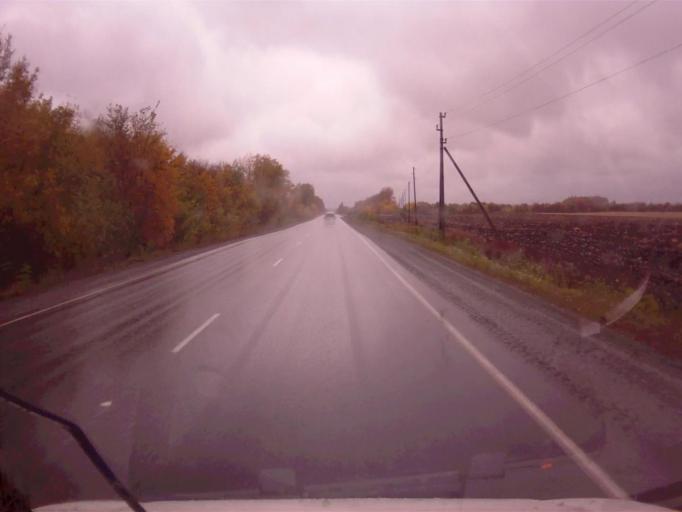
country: RU
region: Chelyabinsk
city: Argayash
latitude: 55.4321
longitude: 60.9862
